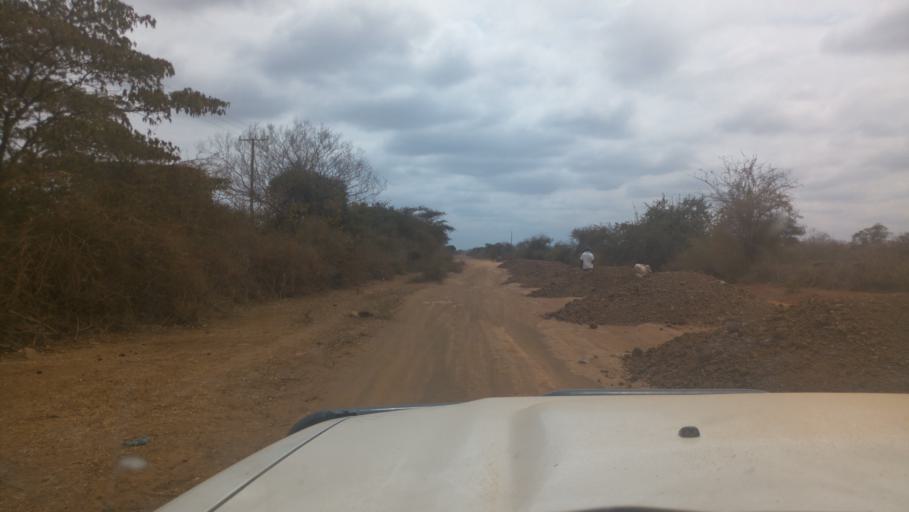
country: KE
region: Makueni
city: Wote
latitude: -1.8499
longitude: 37.9449
